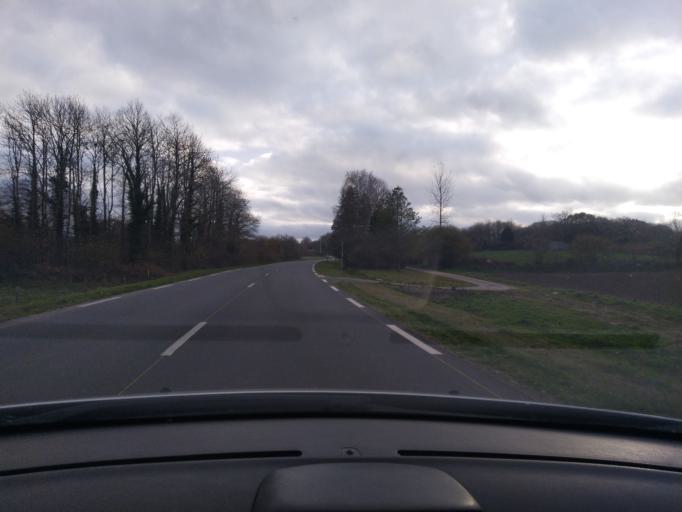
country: FR
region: Brittany
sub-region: Departement des Cotes-d'Armor
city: Plounevez-Moedec
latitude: 48.5690
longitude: -3.4950
